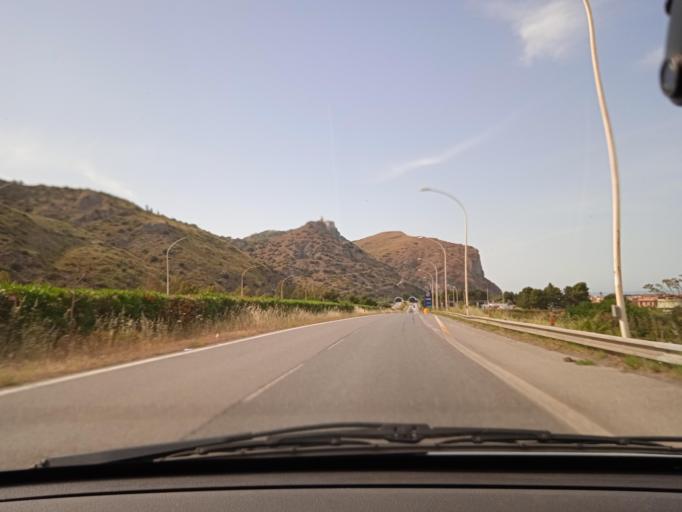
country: IT
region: Sicily
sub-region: Messina
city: Oliveri
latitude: 38.1244
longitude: 15.0542
